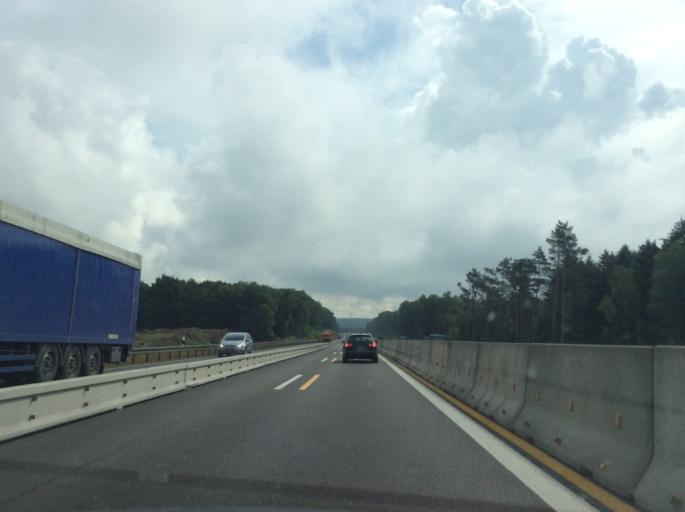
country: DE
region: Brandenburg
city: Rauen
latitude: 52.3124
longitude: 13.9675
